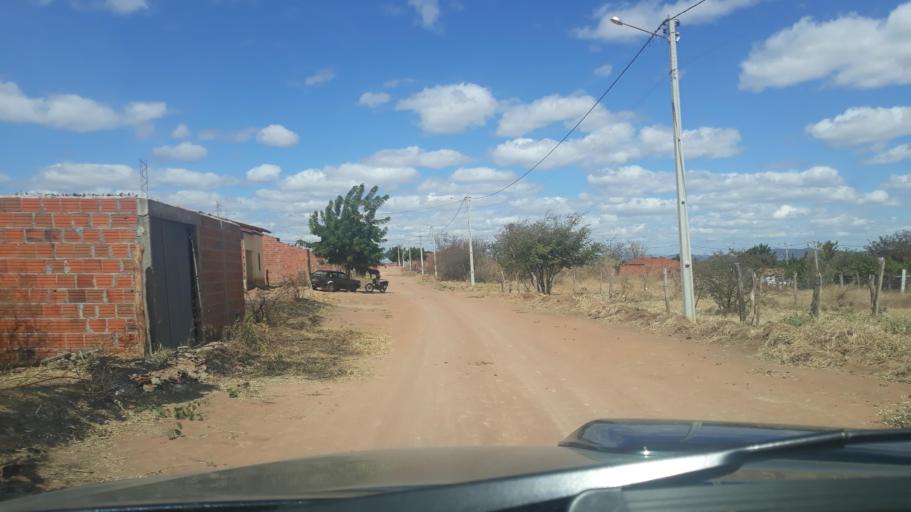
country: BR
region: Bahia
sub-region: Riacho De Santana
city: Riacho de Santana
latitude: -13.9008
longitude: -42.8516
